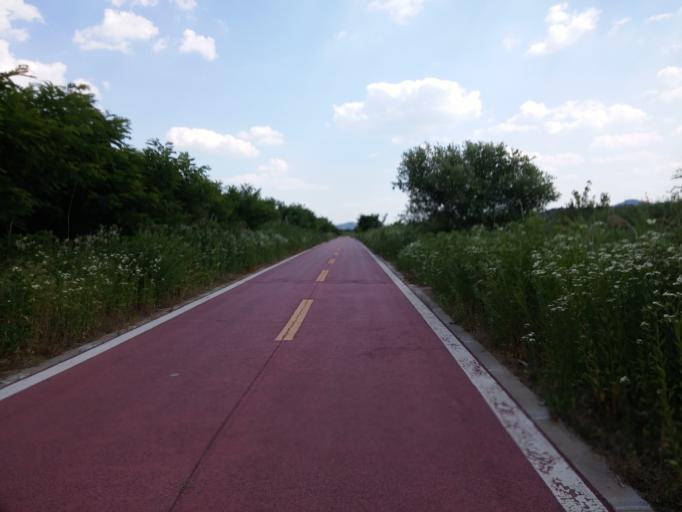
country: KR
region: Chungcheongbuk-do
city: Cheongju-si
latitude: 36.5774
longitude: 127.5043
